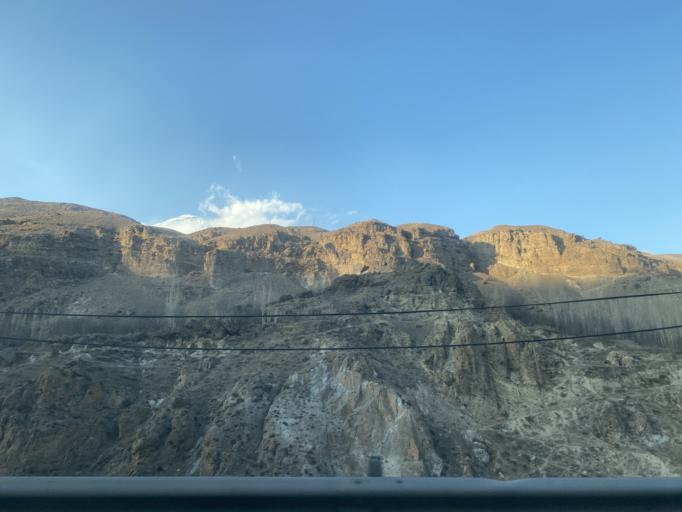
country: IR
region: Tehran
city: Damavand
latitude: 35.8677
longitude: 52.1501
